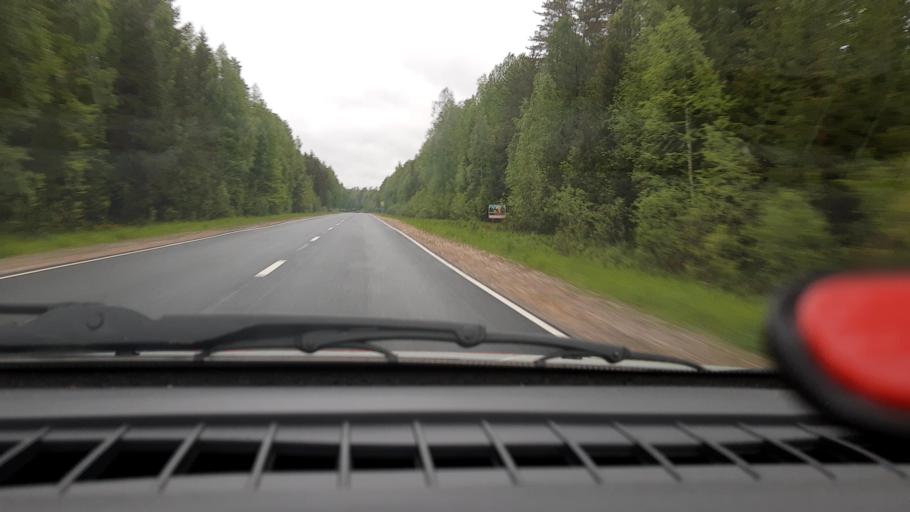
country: RU
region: Nizjnij Novgorod
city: Krasnyye Baki
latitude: 57.1607
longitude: 45.2948
